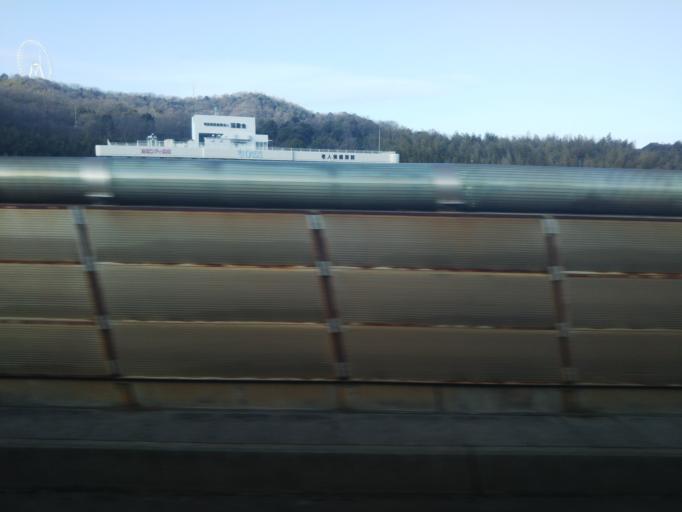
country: JP
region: Kagawa
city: Sakaidecho
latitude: 34.4514
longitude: 133.8075
